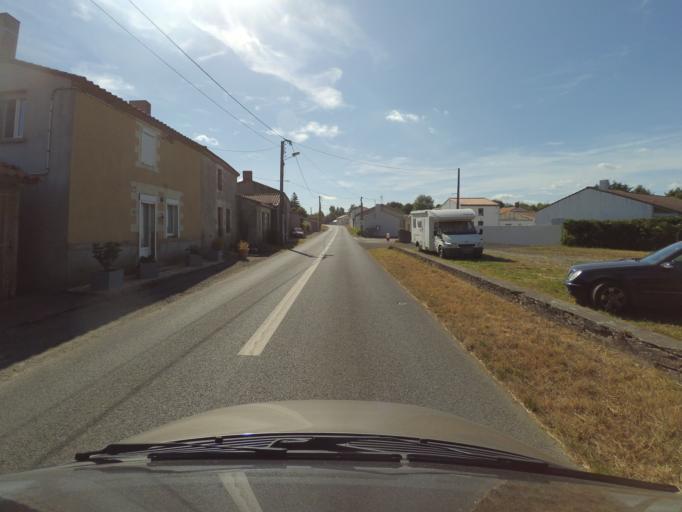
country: FR
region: Pays de la Loire
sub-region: Departement de la Loire-Atlantique
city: Le Bignon
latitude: 47.0913
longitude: -1.5243
